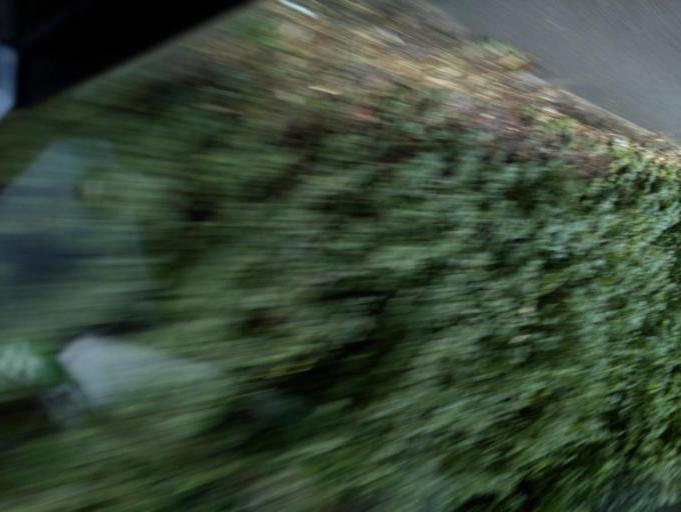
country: GB
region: England
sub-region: Somerset
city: Yeovil
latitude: 50.9337
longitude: -2.6418
